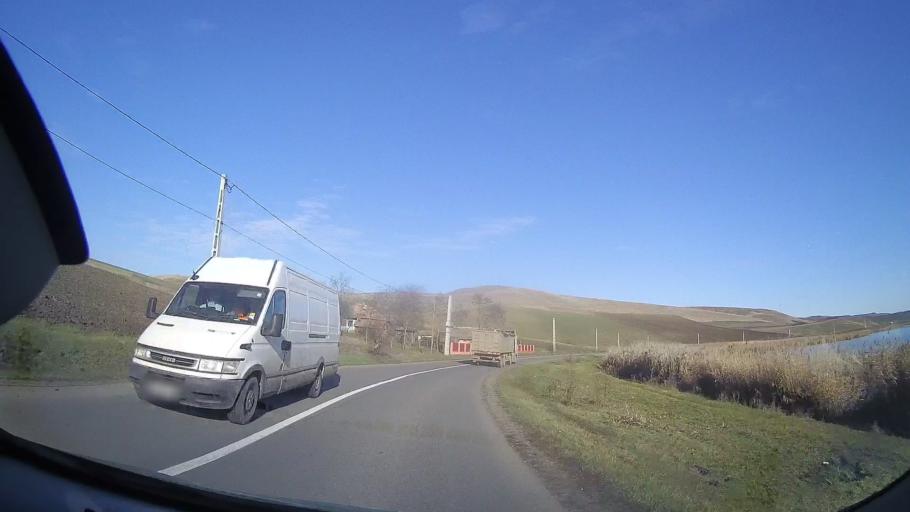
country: RO
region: Mures
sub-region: Comuna Mihesu de Campie
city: Mihesu de Campie
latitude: 46.6470
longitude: 24.1469
